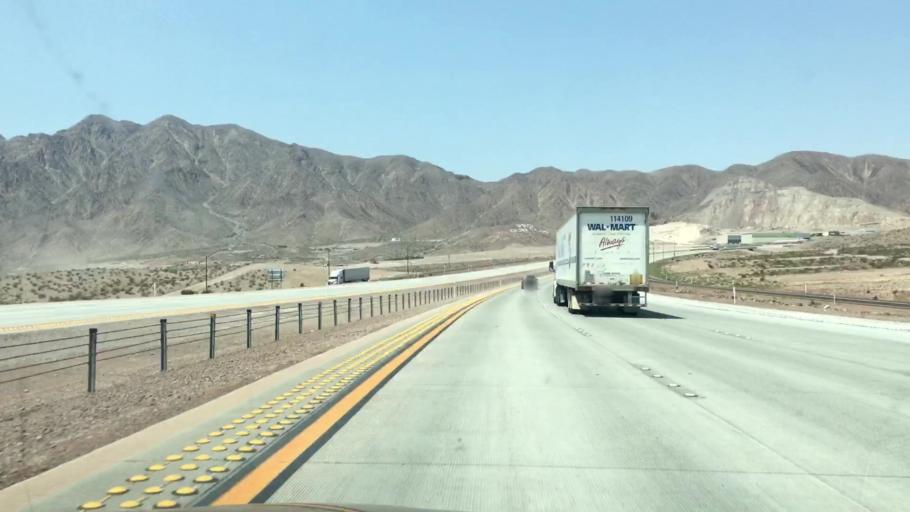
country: US
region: Nevada
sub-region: Clark County
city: Boulder City
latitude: 35.9529
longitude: -114.9032
